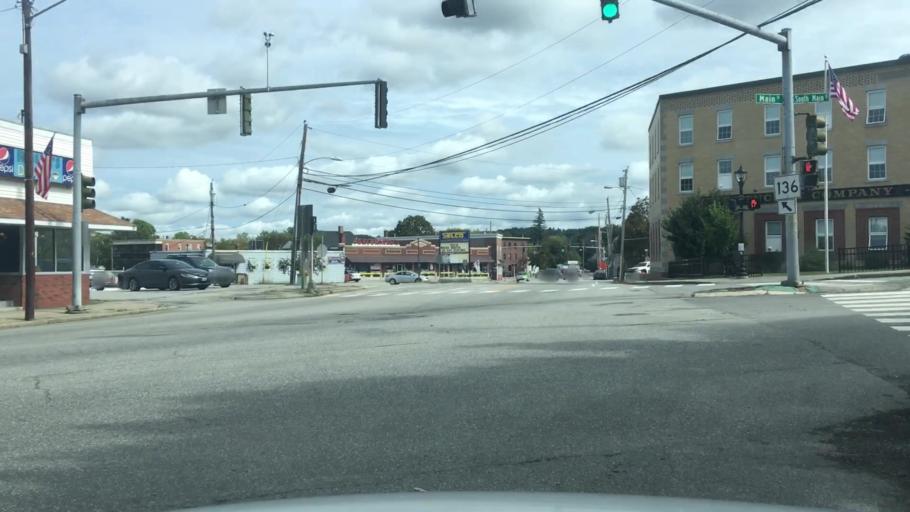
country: US
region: Maine
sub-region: Androscoggin County
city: Auburn
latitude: 44.0876
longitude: -70.2251
